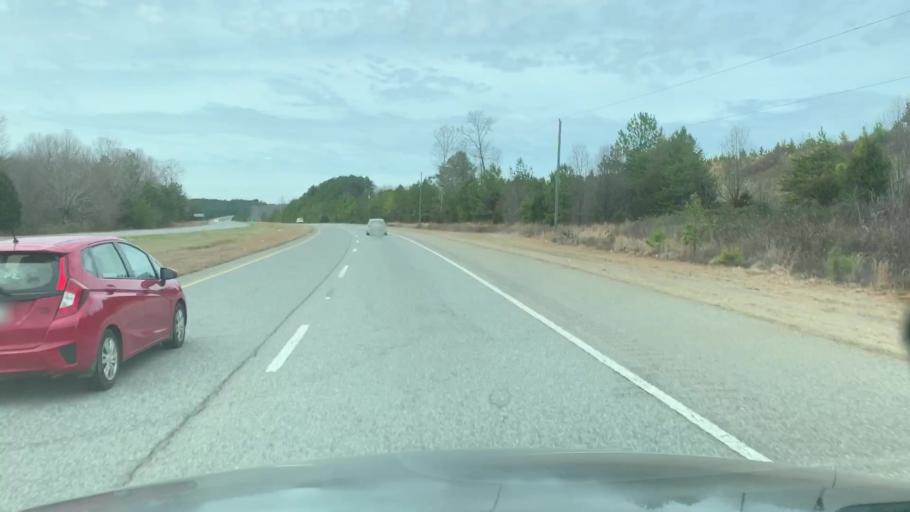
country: US
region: South Carolina
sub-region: Greenville County
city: Golden Grove
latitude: 34.7283
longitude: -82.4065
